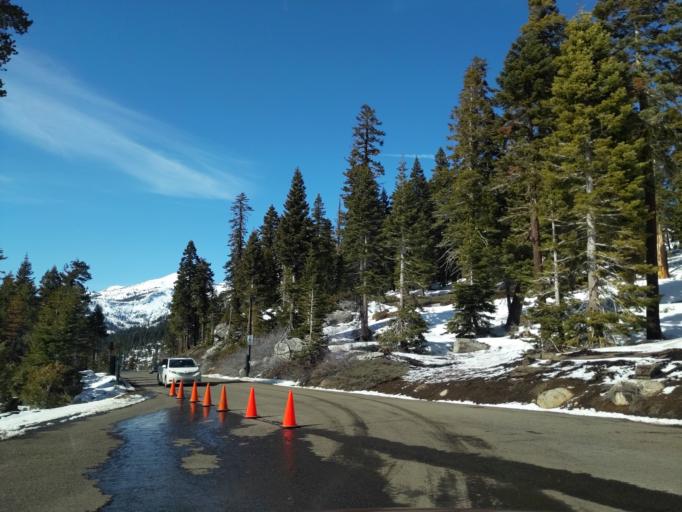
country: US
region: California
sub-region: El Dorado County
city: South Lake Tahoe
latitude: 38.8036
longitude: -120.0842
